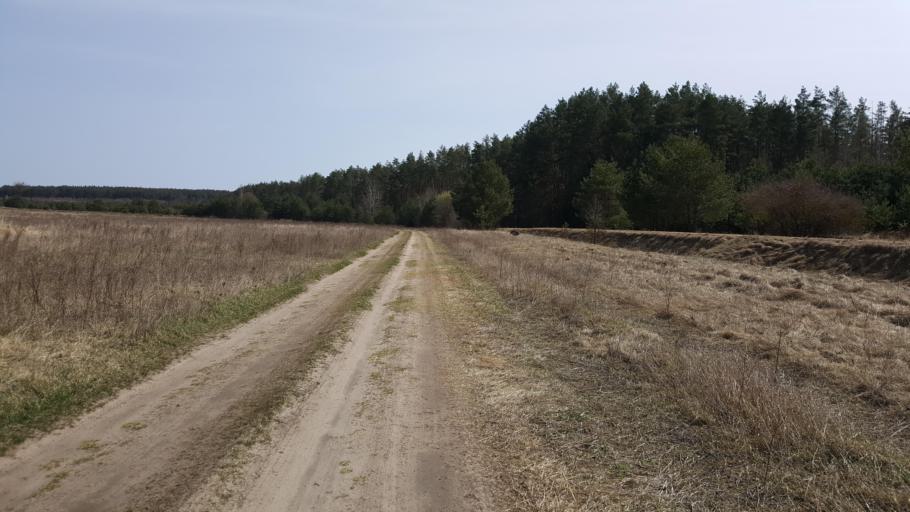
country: BY
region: Brest
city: Kamyanyuki
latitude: 52.5637
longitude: 23.7597
